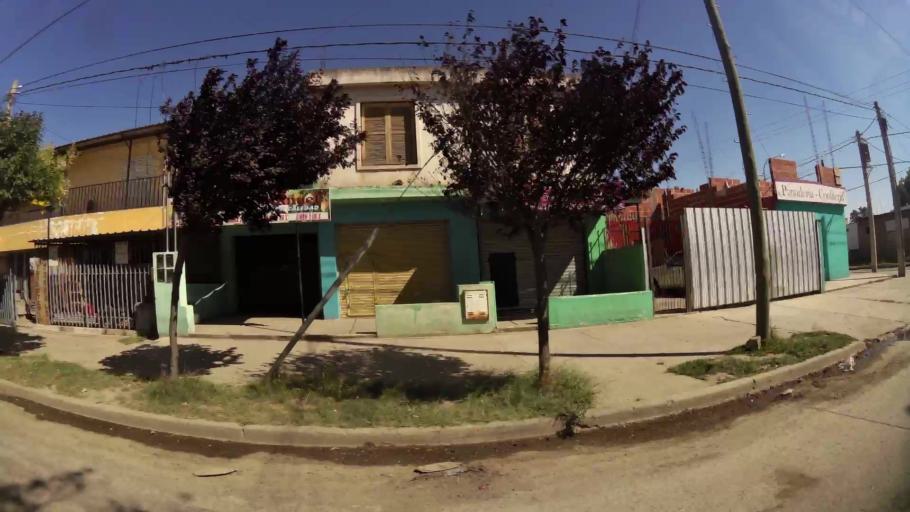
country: AR
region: Cordoba
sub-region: Departamento de Capital
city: Cordoba
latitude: -31.3674
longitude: -64.1569
